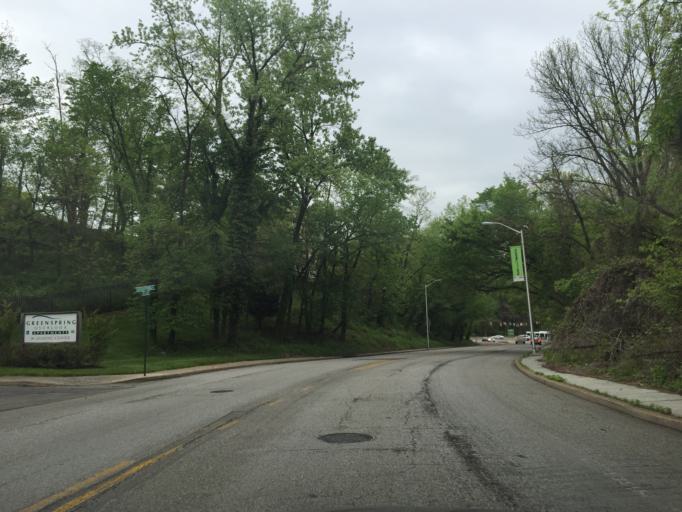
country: US
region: Maryland
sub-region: Baltimore County
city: Lochearn
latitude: 39.3389
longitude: -76.6577
